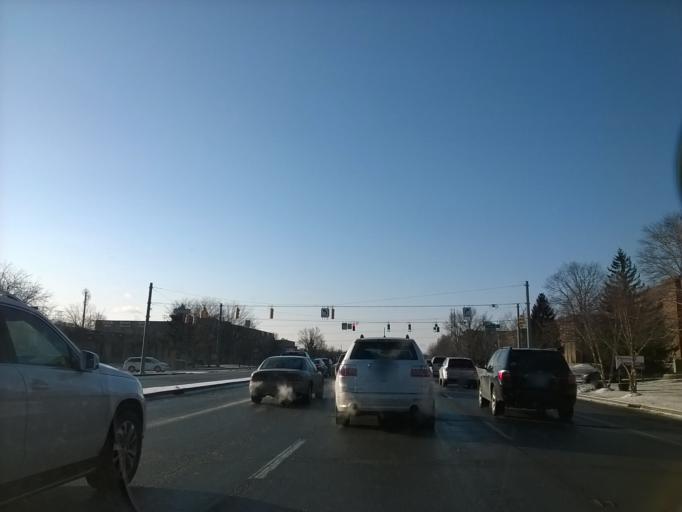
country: US
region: Indiana
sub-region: Marion County
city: Meridian Hills
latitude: 39.9239
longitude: -86.1581
